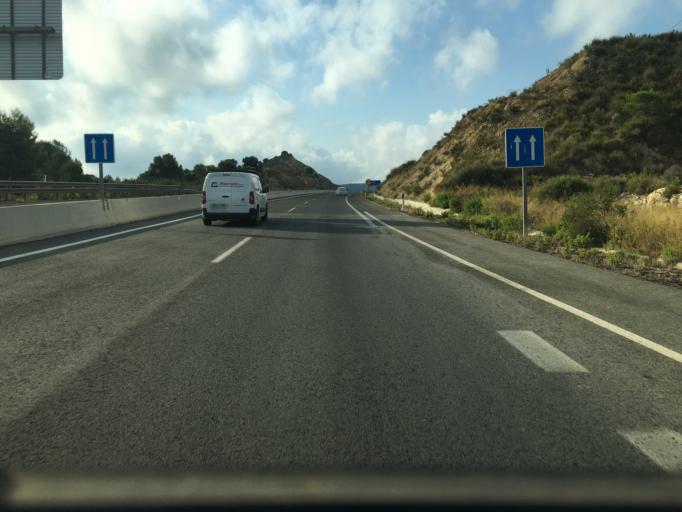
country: ES
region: Murcia
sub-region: Murcia
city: Beniel
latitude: 37.9602
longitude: -0.9626
